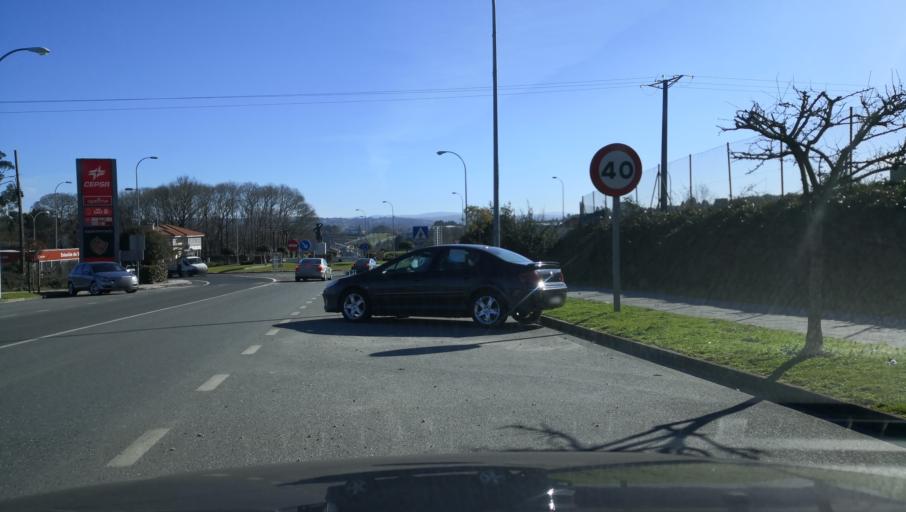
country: ES
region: Galicia
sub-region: Provincia de Pontevedra
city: Silleda
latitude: 42.6958
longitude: -8.2413
